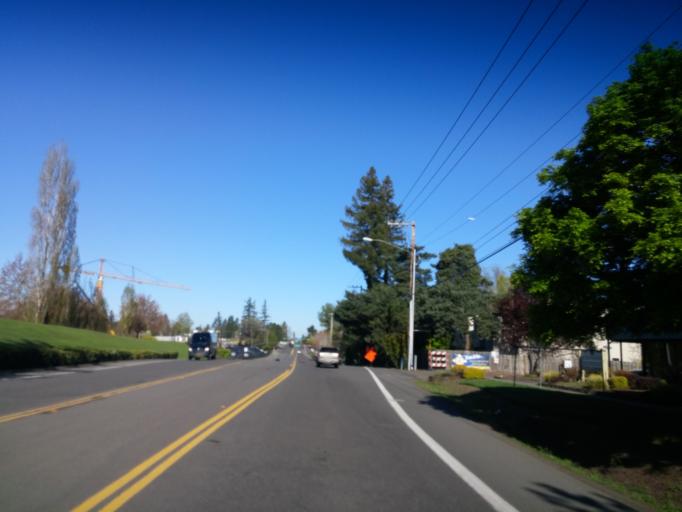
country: US
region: Oregon
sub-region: Washington County
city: Cedar Mill
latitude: 45.5130
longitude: -122.8261
